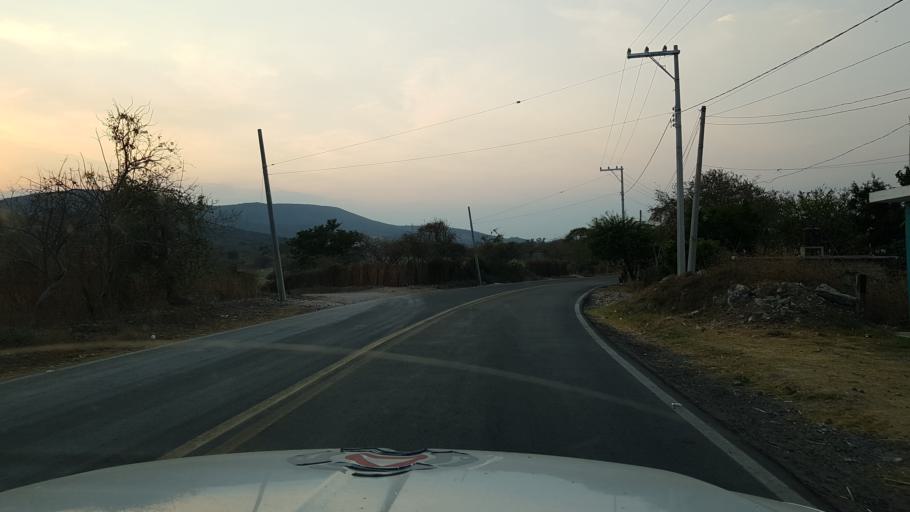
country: MX
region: Morelos
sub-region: Ayala
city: Olintepec
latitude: 18.7311
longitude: -99.0047
